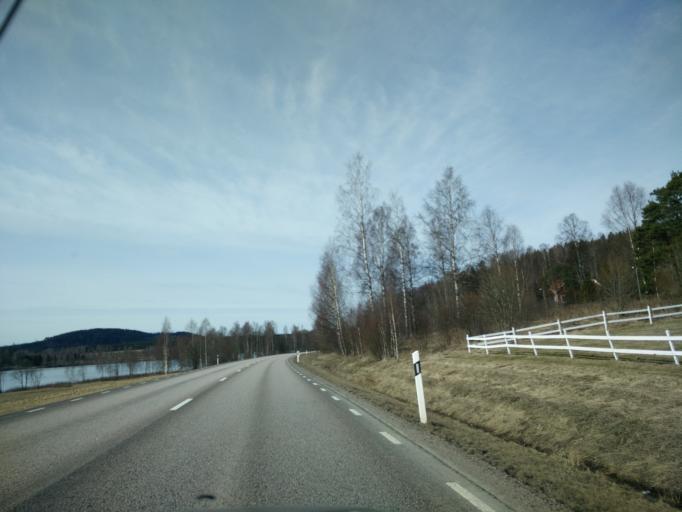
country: SE
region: Vaermland
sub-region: Hagfors Kommun
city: Hagfors
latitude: 60.0289
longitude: 13.6109
